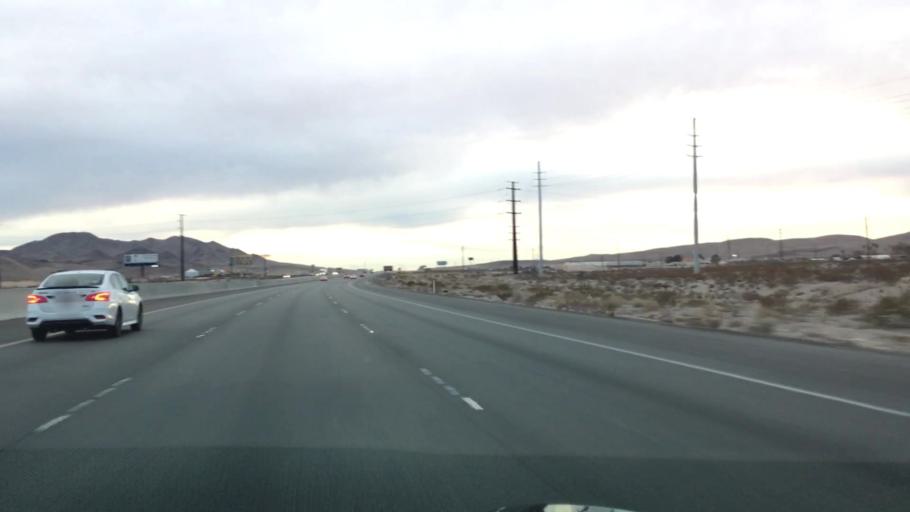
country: US
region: Nevada
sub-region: Clark County
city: Enterprise
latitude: 35.9427
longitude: -115.1855
